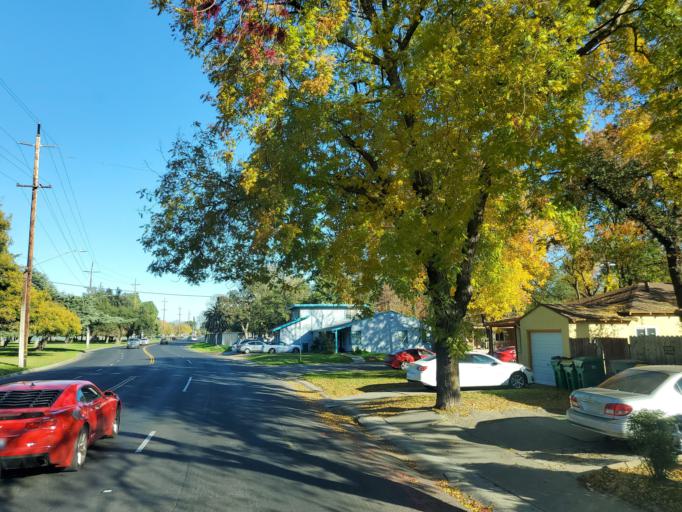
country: US
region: California
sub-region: San Joaquin County
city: Stockton
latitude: 37.9818
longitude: -121.2925
